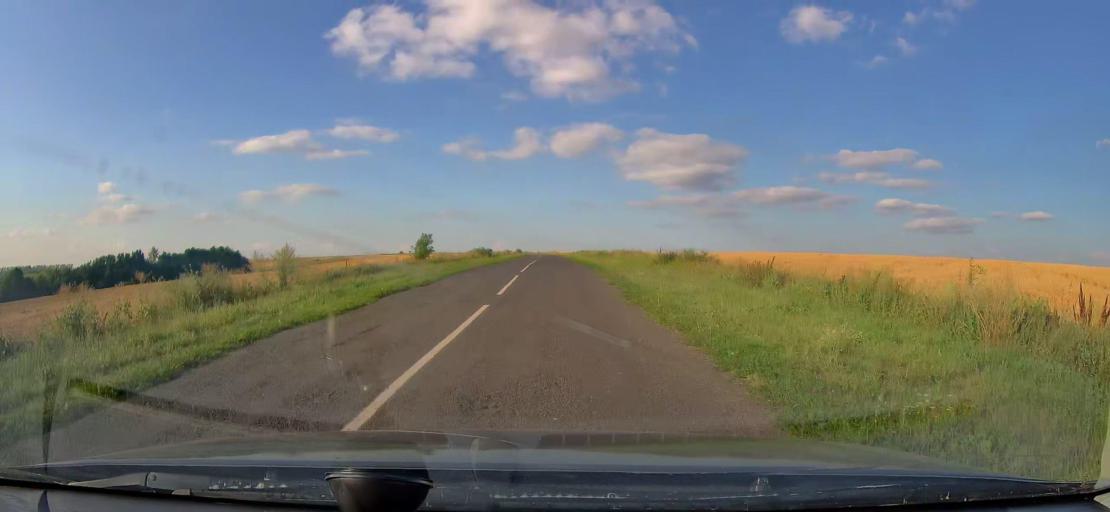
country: RU
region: Kursk
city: Zolotukhino
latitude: 52.0288
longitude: 36.2146
